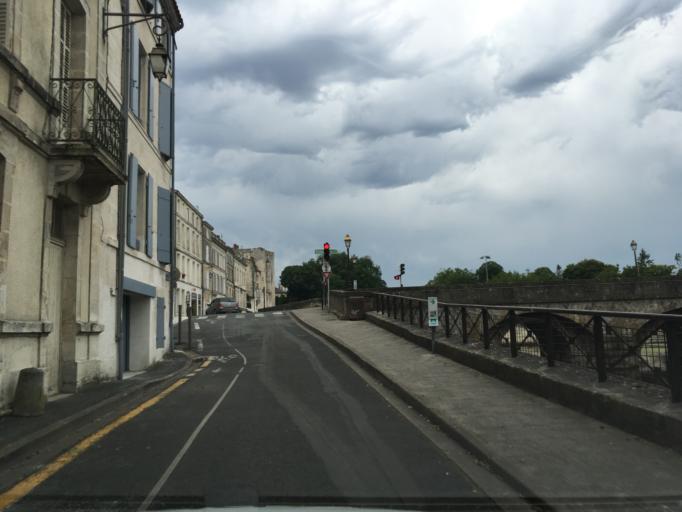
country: FR
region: Poitou-Charentes
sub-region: Departement des Deux-Sevres
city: Niort
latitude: 46.3273
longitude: -0.4639
